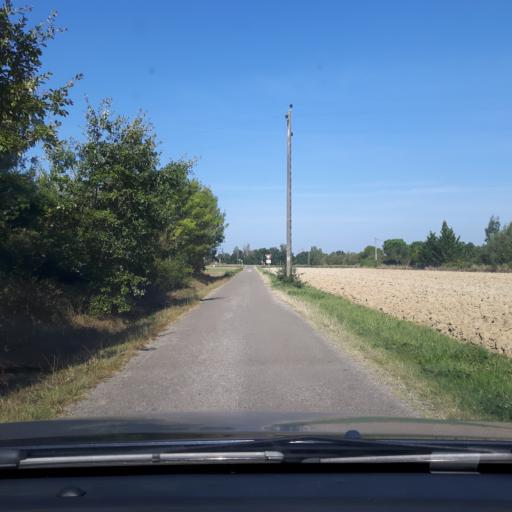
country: FR
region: Midi-Pyrenees
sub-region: Departement de la Haute-Garonne
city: Paulhac
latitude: 43.7812
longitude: 1.5613
